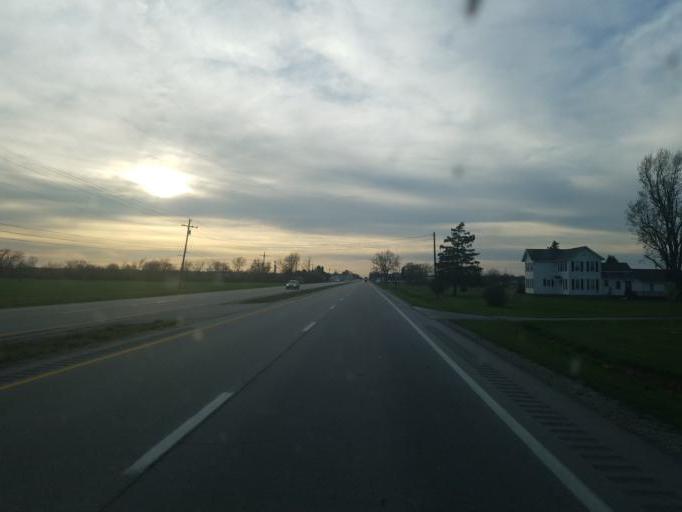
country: US
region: Ohio
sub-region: Sandusky County
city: Gibsonburg
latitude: 41.4216
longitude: -83.2915
